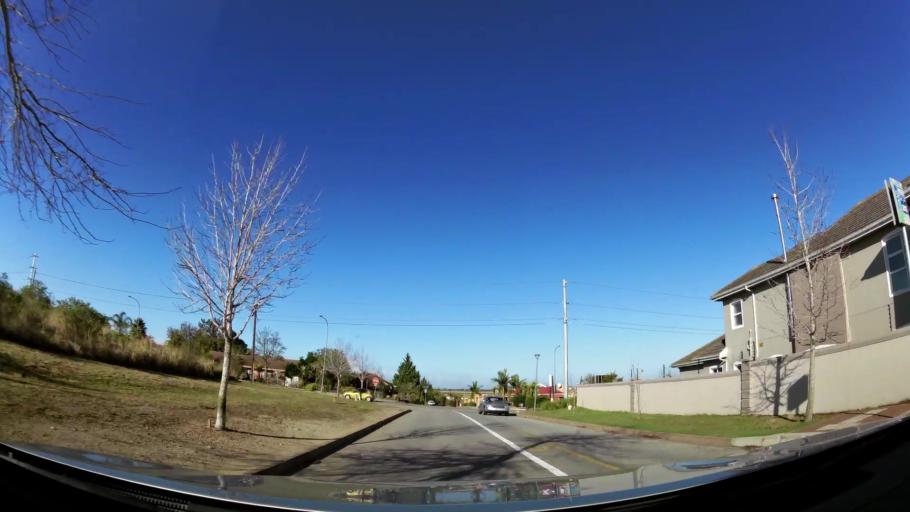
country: ZA
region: Western Cape
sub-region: Eden District Municipality
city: George
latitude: -33.9671
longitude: 22.4381
